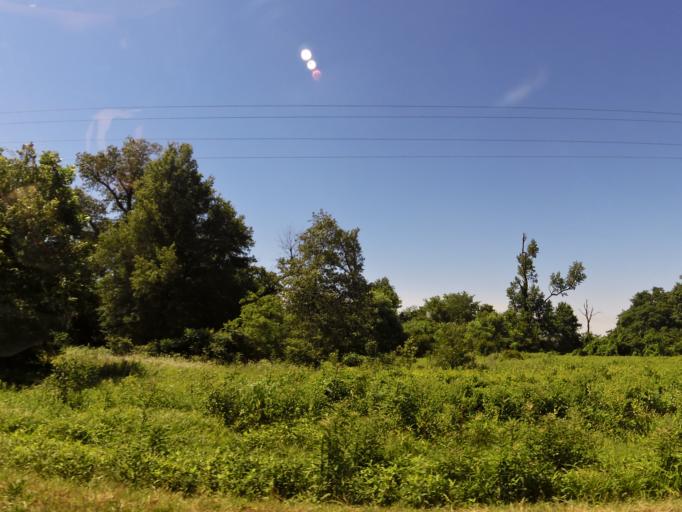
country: US
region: Missouri
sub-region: New Madrid County
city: Portageville
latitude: 36.5538
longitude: -89.7705
